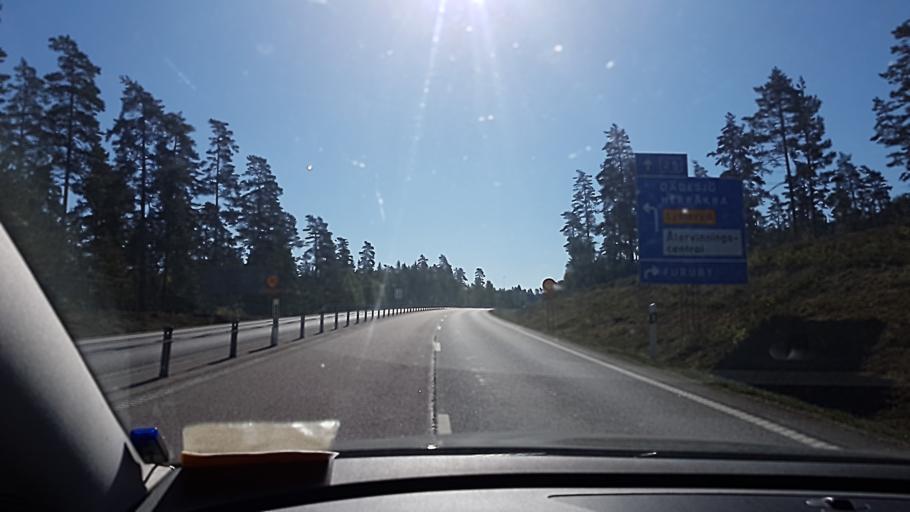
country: SE
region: Kronoberg
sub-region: Lessebo Kommun
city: Hovmantorp
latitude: 56.8624
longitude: 15.0323
